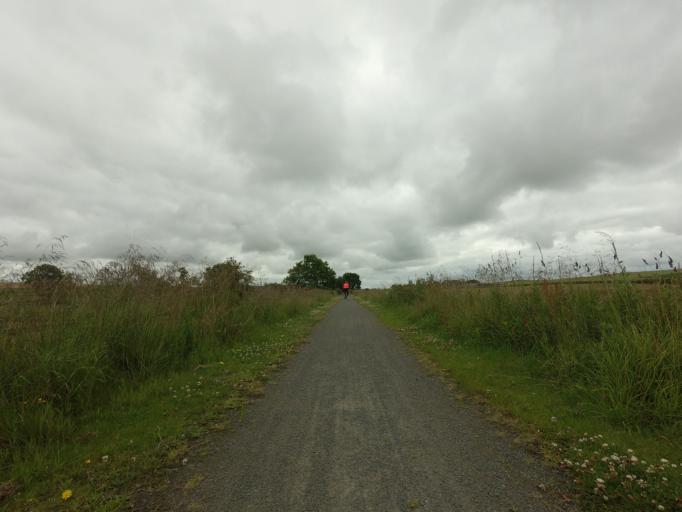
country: GB
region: Scotland
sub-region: Aberdeenshire
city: Ellon
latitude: 57.4740
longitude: -2.1257
